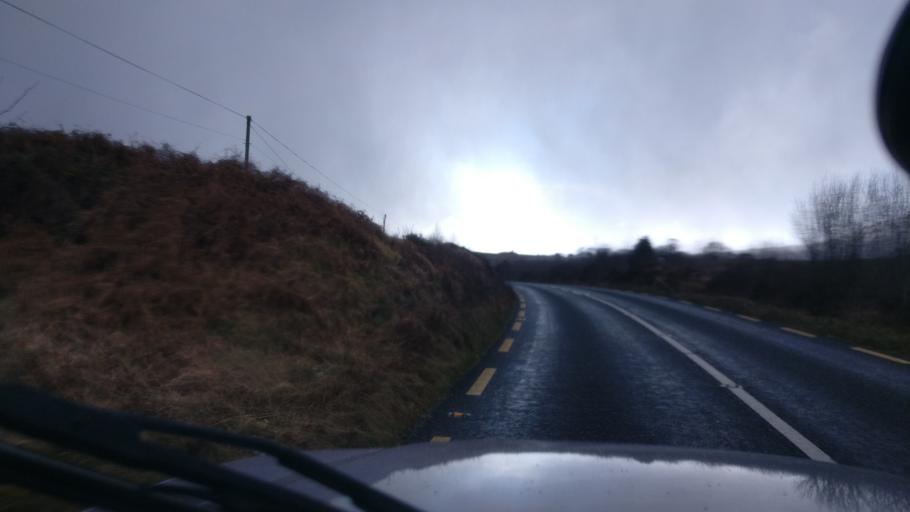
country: IE
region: Connaught
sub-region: County Galway
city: Oughterard
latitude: 53.4519
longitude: -9.5768
